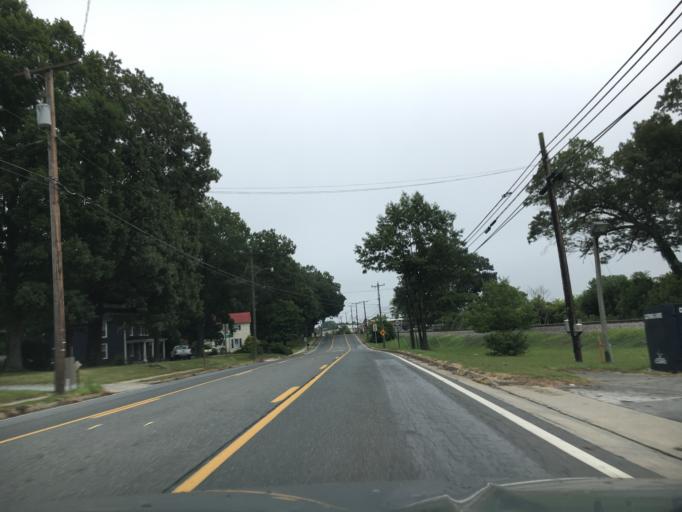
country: US
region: Virginia
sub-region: Campbell County
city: Brookneal
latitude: 37.0544
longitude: -78.9480
